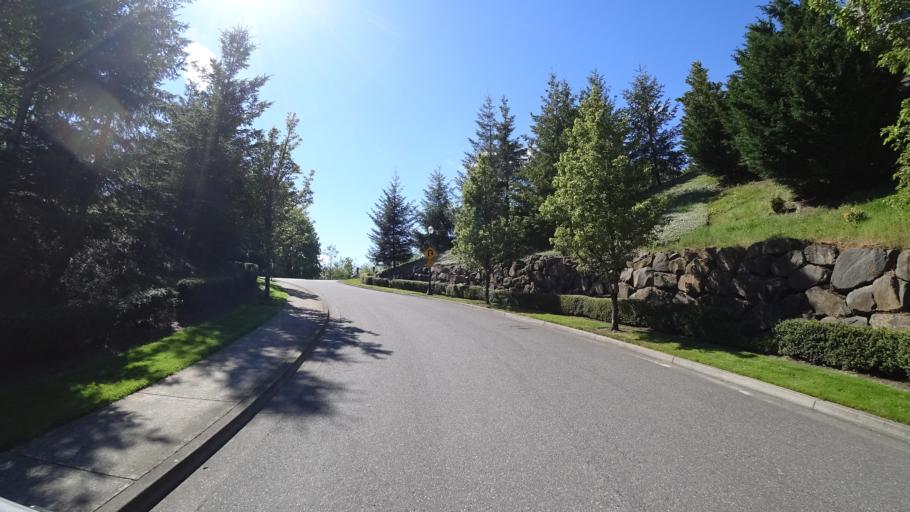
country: US
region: Oregon
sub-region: Washington County
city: West Haven
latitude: 45.5486
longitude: -122.7799
